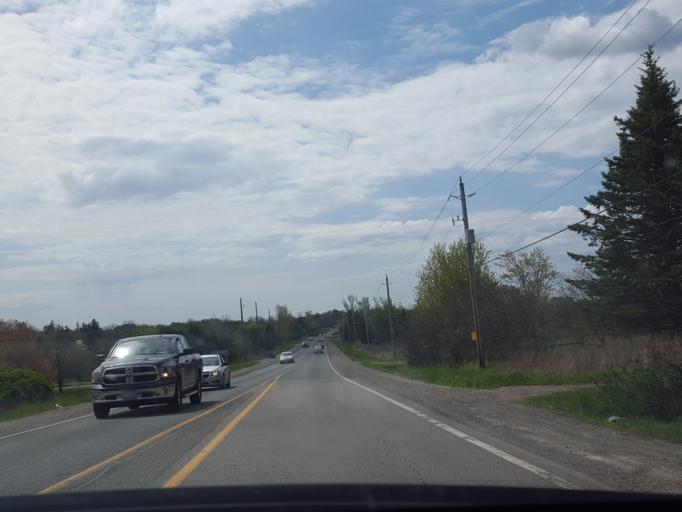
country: CA
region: Ontario
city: Oshawa
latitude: 43.9209
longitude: -78.7062
